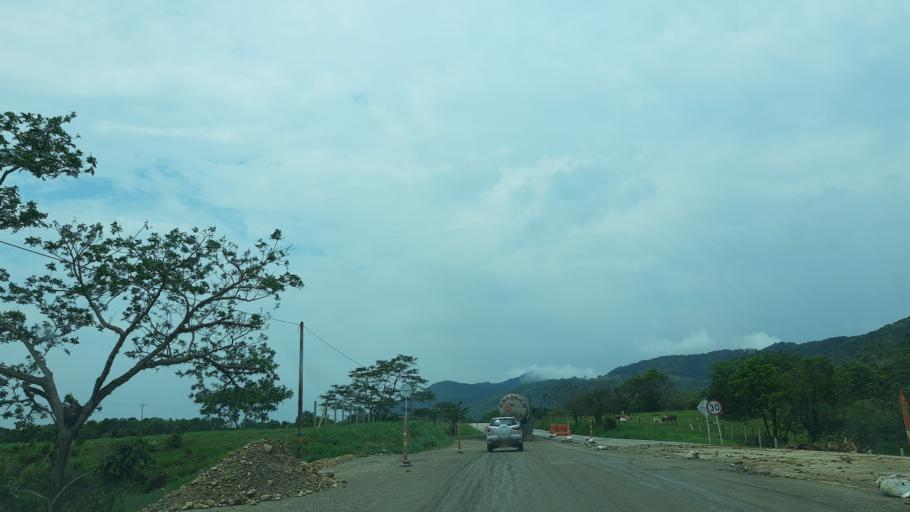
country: CO
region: Casanare
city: Sabanalarga
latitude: 4.7810
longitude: -72.9994
